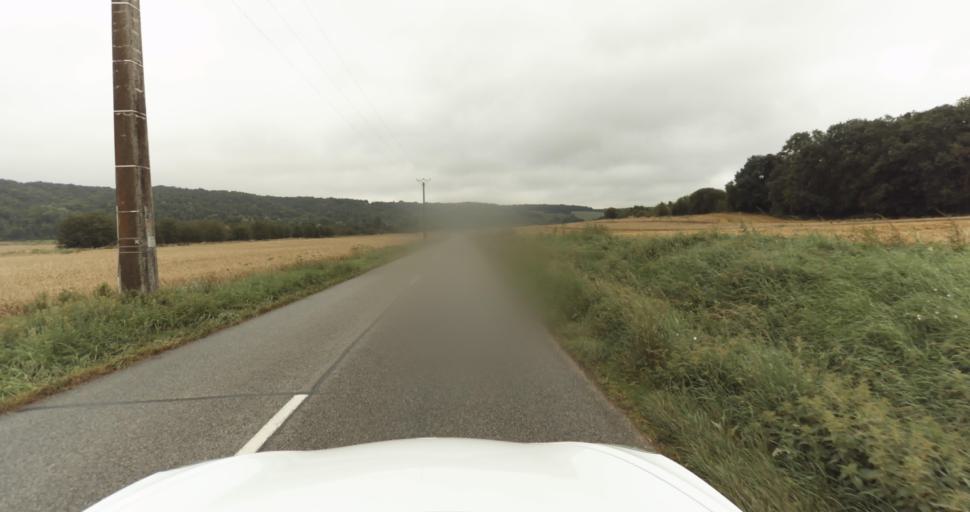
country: FR
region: Haute-Normandie
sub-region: Departement de l'Eure
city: Normanville
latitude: 49.0973
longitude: 1.1232
